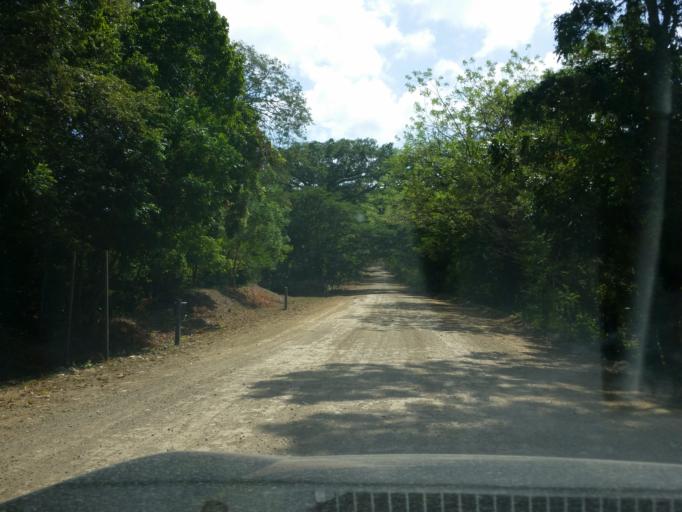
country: NI
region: Rivas
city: San Juan del Sur
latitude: 11.1388
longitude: -85.7836
